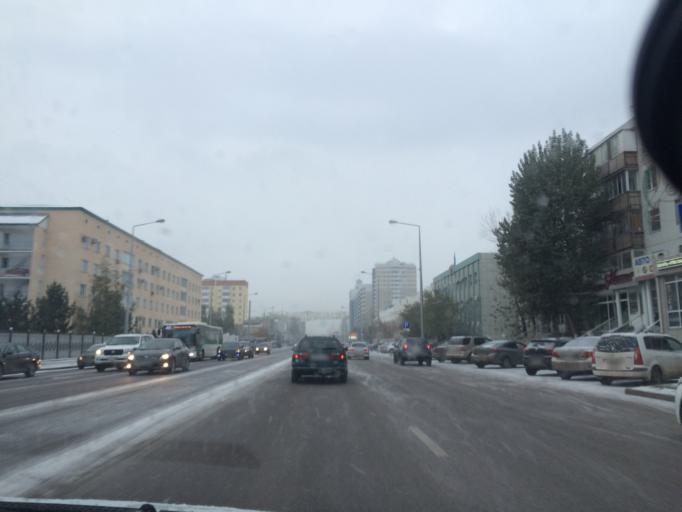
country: KZ
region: Astana Qalasy
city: Astana
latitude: 51.1721
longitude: 71.4072
